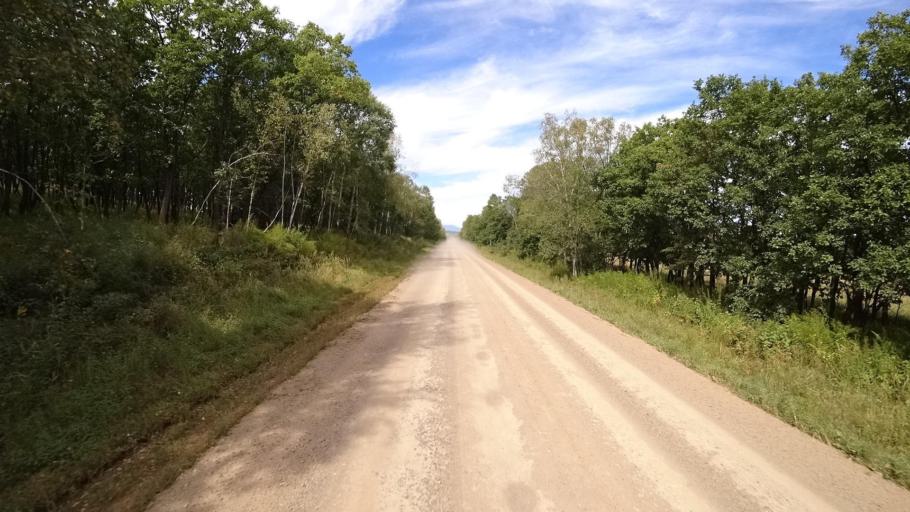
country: RU
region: Primorskiy
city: Yakovlevka
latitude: 44.6080
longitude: 133.6013
